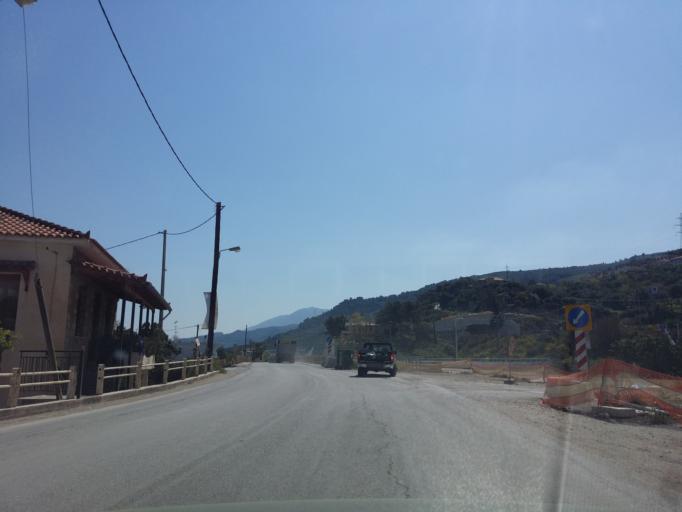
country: GR
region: West Greece
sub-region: Nomos Achaias
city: Aiyira
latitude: 38.1463
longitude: 22.3618
